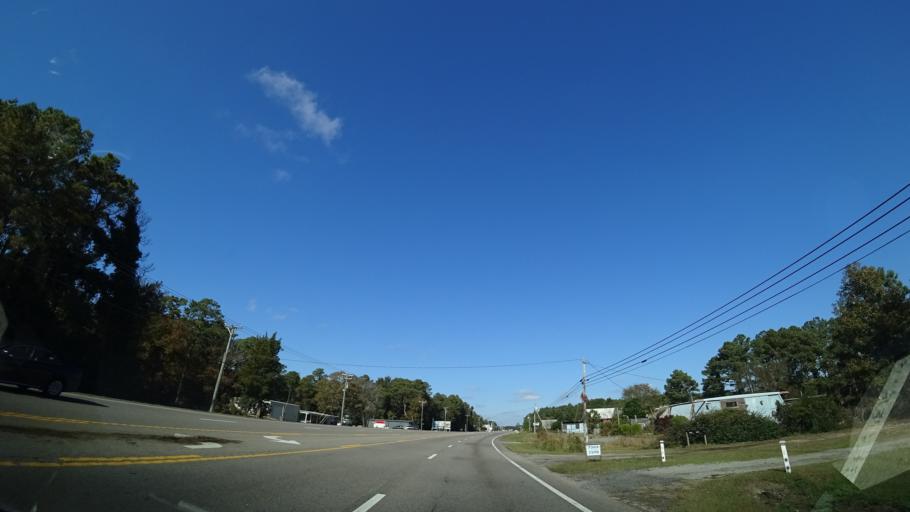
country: US
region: North Carolina
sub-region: Dare County
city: Southern Shores
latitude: 36.1810
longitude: -75.8643
